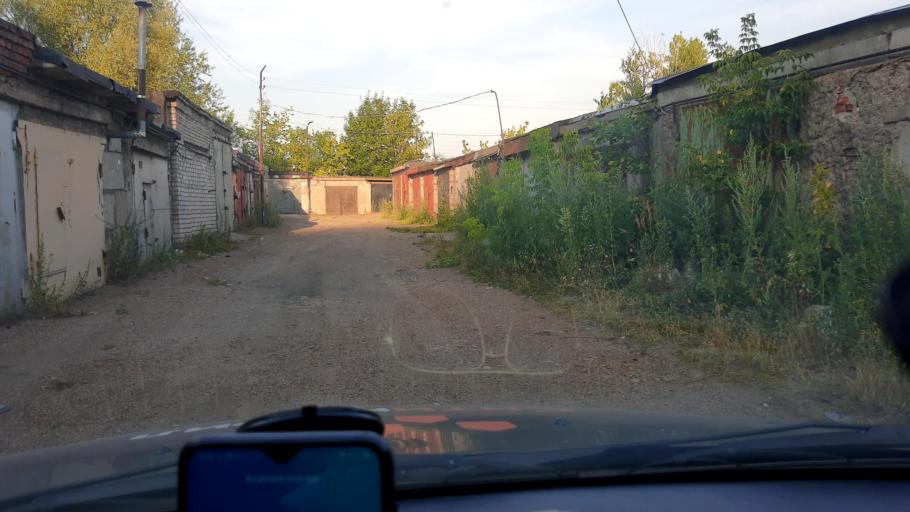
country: RU
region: Bashkortostan
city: Ufa
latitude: 54.8109
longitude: 56.1487
